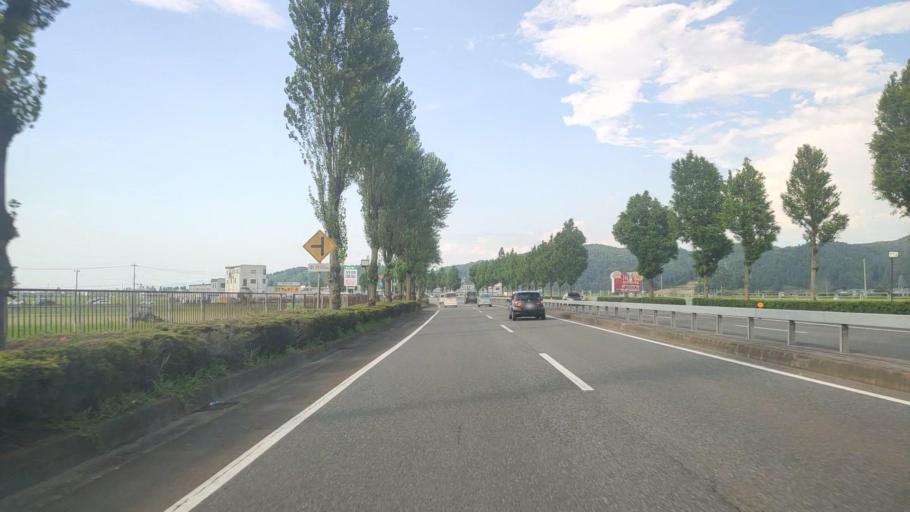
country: JP
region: Fukui
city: Sabae
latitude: 35.9917
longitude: 136.2026
